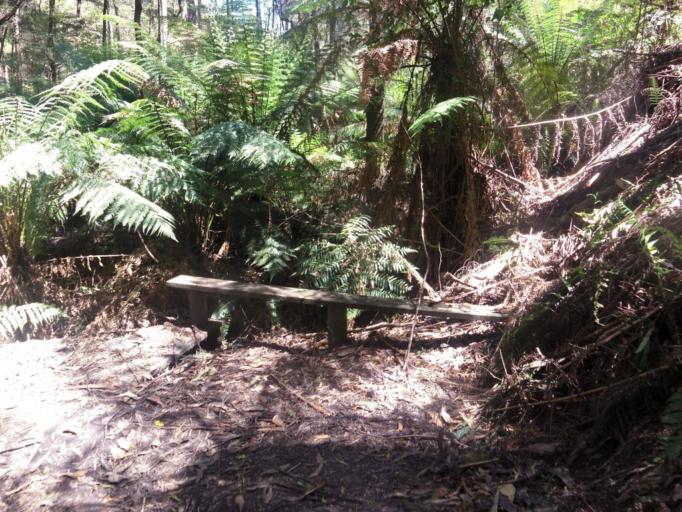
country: AU
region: Victoria
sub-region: Yarra Ranges
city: Millgrove
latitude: -37.8654
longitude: 145.7593
